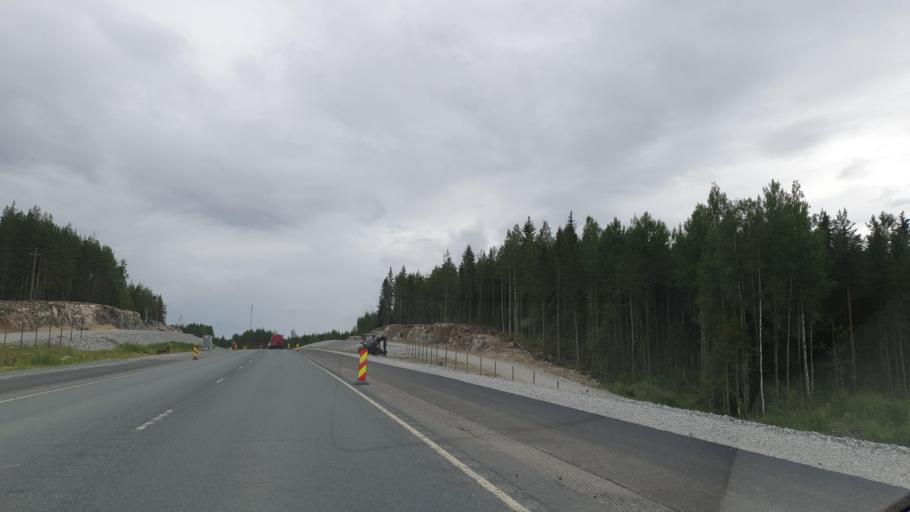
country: FI
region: Northern Savo
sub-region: Ylae-Savo
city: Lapinlahti
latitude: 63.2842
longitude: 27.4552
